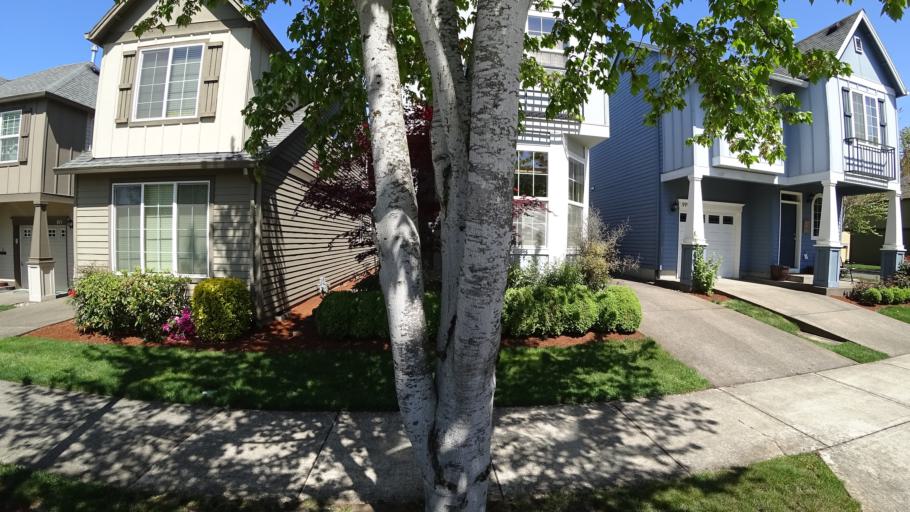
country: US
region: Oregon
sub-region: Washington County
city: Hillsboro
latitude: 45.5098
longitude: -122.9758
